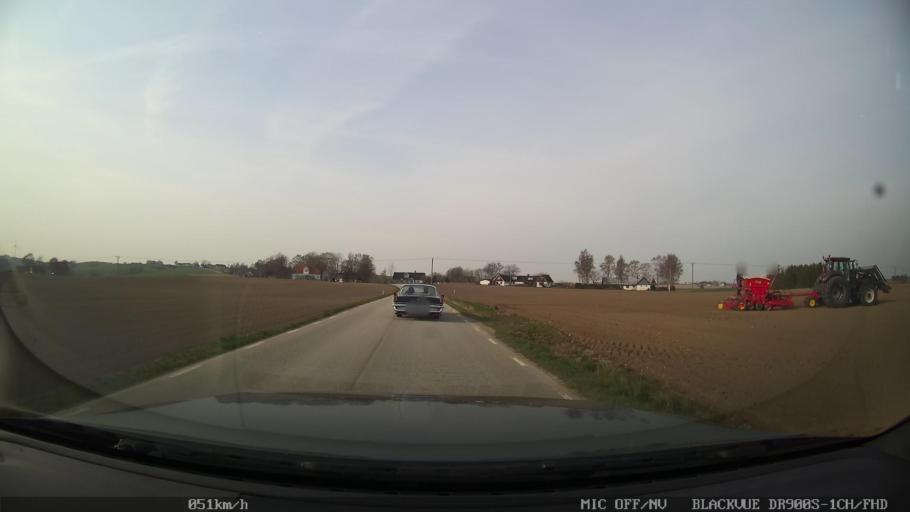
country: SE
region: Skane
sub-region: Ystads Kommun
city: Ystad
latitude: 55.4616
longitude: 13.8248
